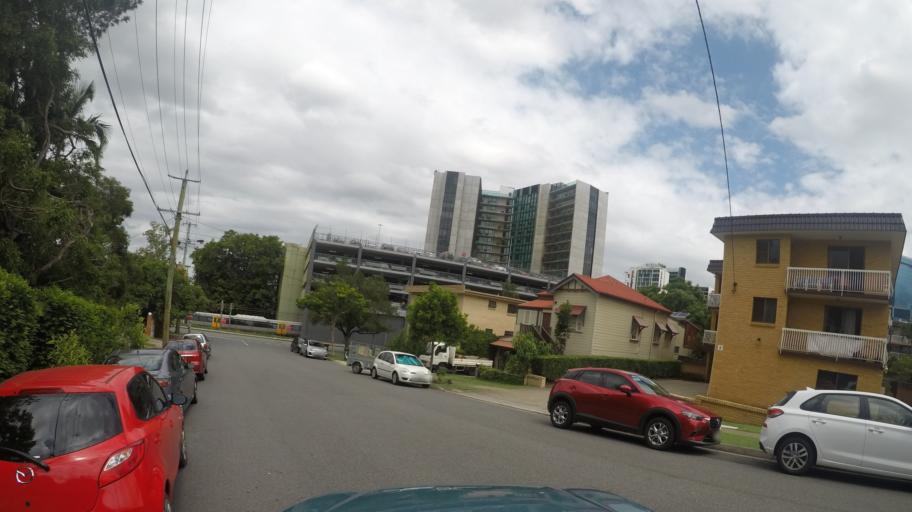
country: AU
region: Queensland
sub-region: Brisbane
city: Toowong
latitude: -27.4830
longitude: 152.9935
